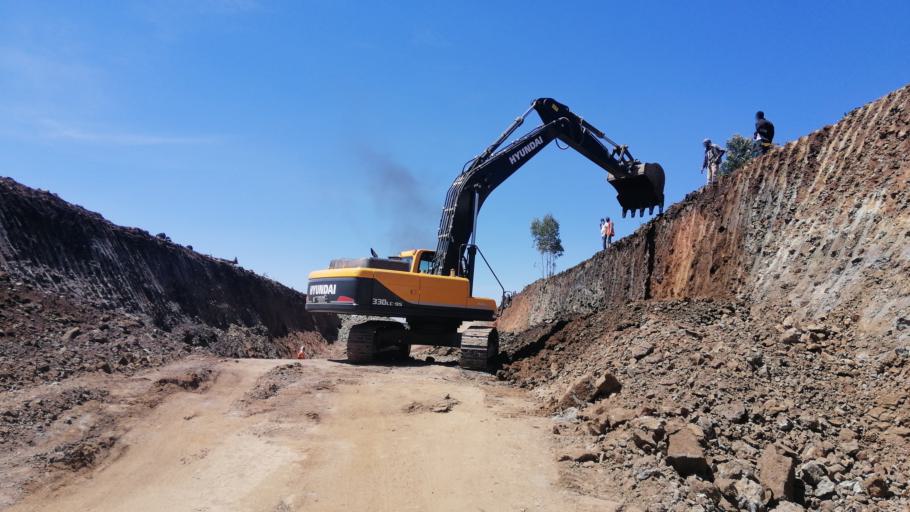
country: ET
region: Amhara
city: Debre Tabor
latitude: 11.4196
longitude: 38.2172
